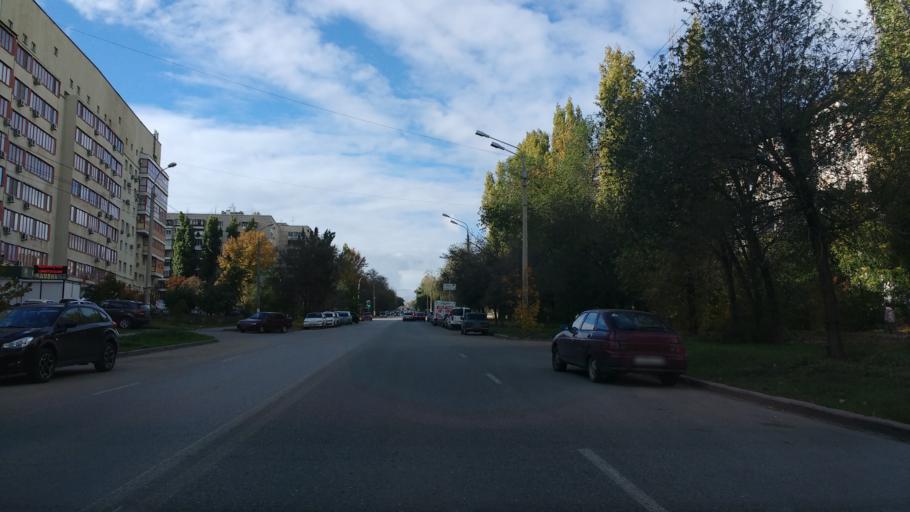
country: RU
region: Volgograd
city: Krasnoslobodsk
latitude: 48.7728
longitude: 44.5621
